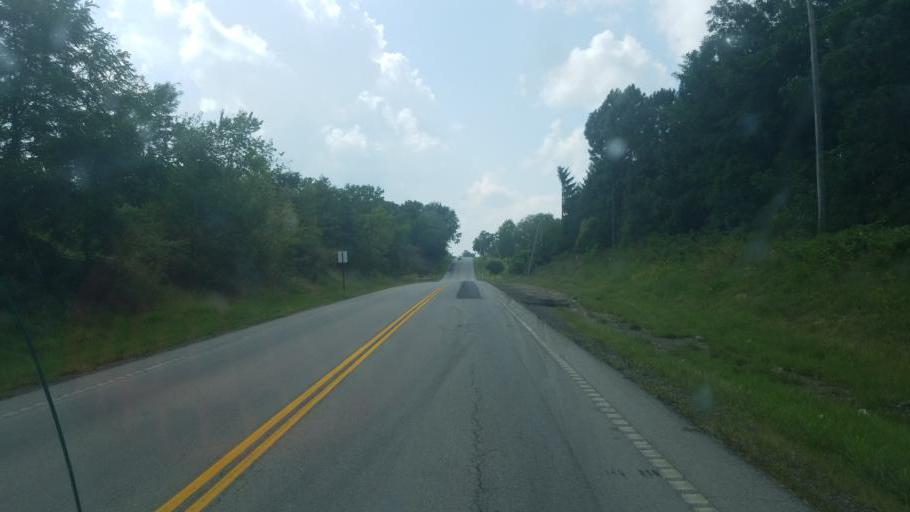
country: US
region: Ohio
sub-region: Huron County
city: New London
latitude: 41.0292
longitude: -82.4305
